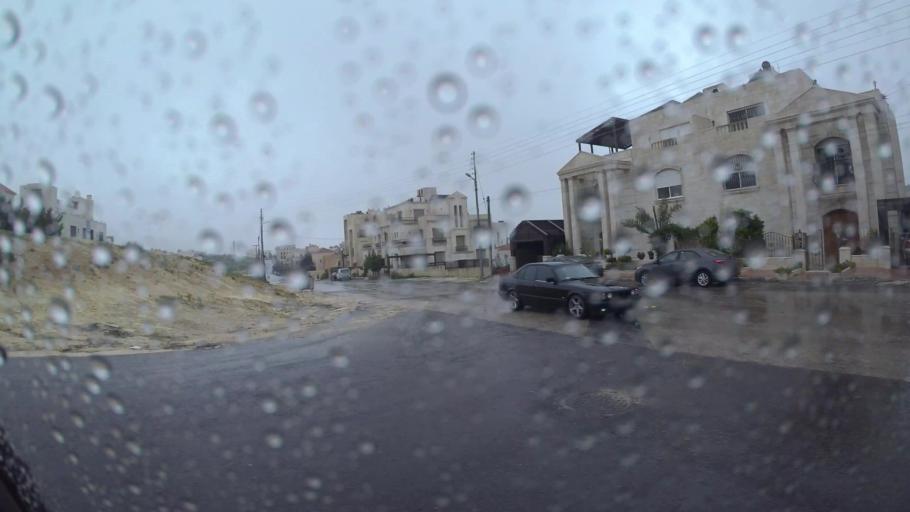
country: JO
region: Amman
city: Al Jubayhah
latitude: 32.0072
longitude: 35.8248
